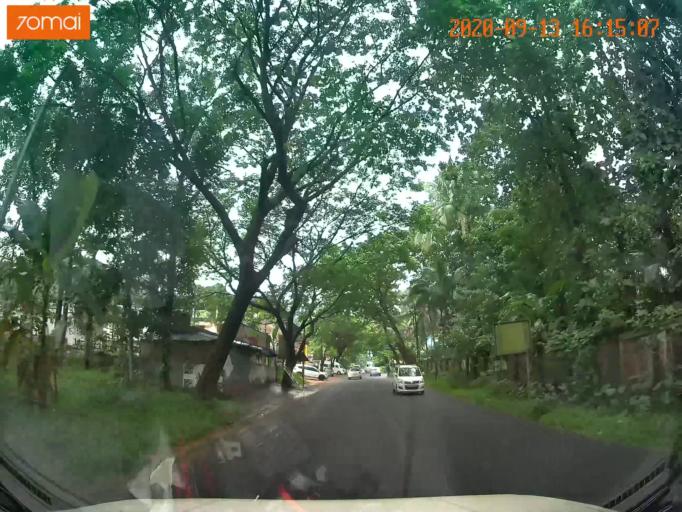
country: IN
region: Kerala
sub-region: Kottayam
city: Palackattumala
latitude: 9.6913
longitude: 76.6399
